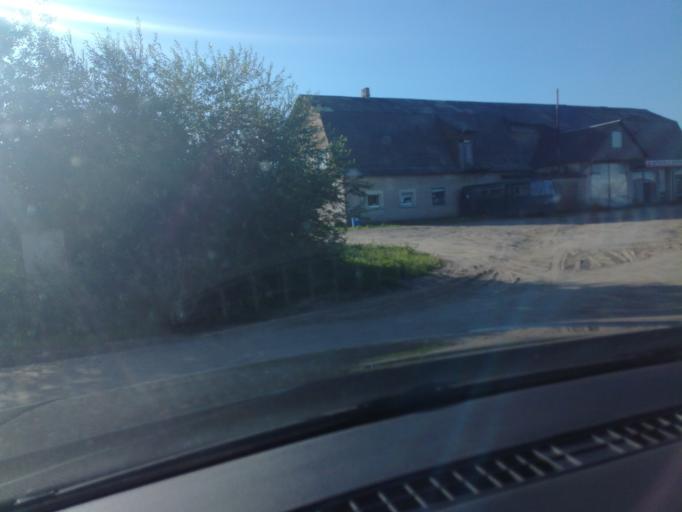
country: LT
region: Alytaus apskritis
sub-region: Alytus
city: Alytus
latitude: 54.4049
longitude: 23.9964
